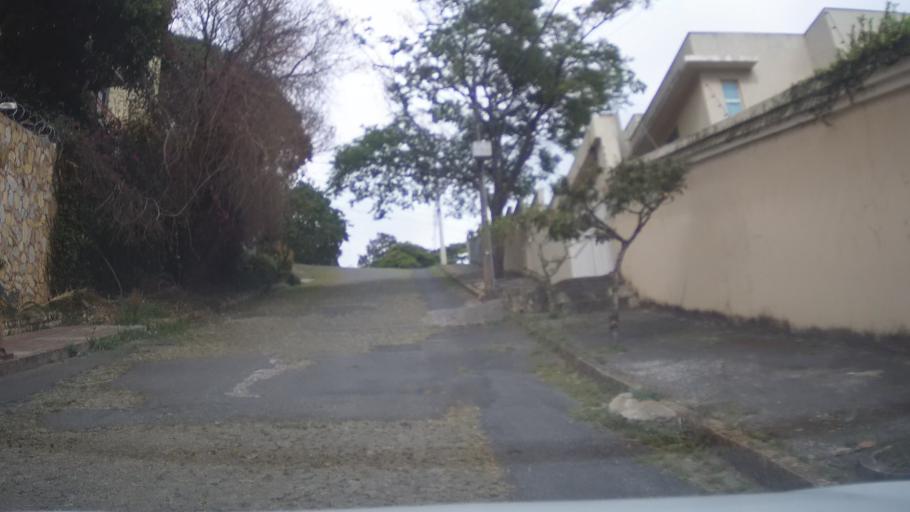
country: BR
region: Minas Gerais
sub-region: Belo Horizonte
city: Belo Horizonte
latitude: -19.9548
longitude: -43.9220
